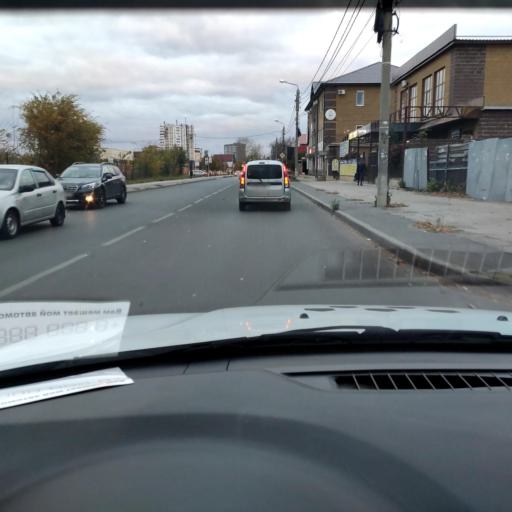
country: RU
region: Samara
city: Tol'yatti
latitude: 53.5166
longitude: 49.4089
